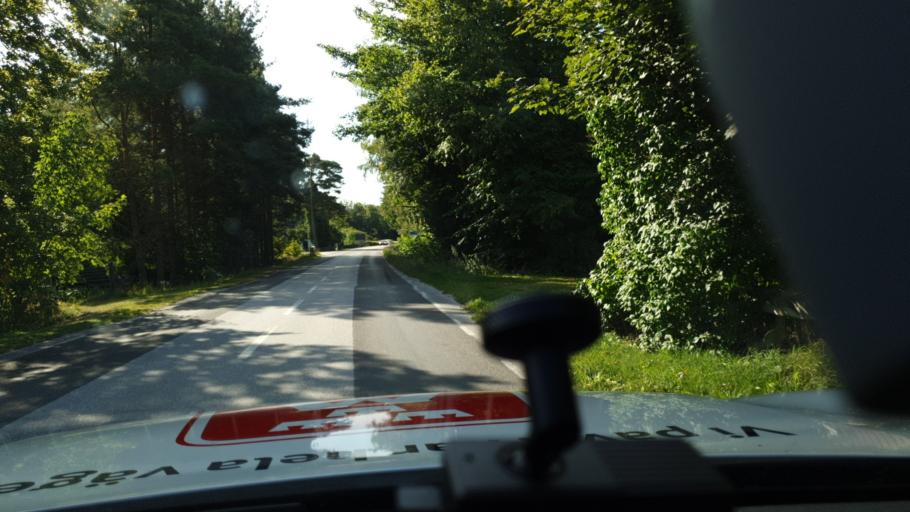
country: SE
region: Gotland
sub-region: Gotland
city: Hemse
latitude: 57.0948
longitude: 18.3039
